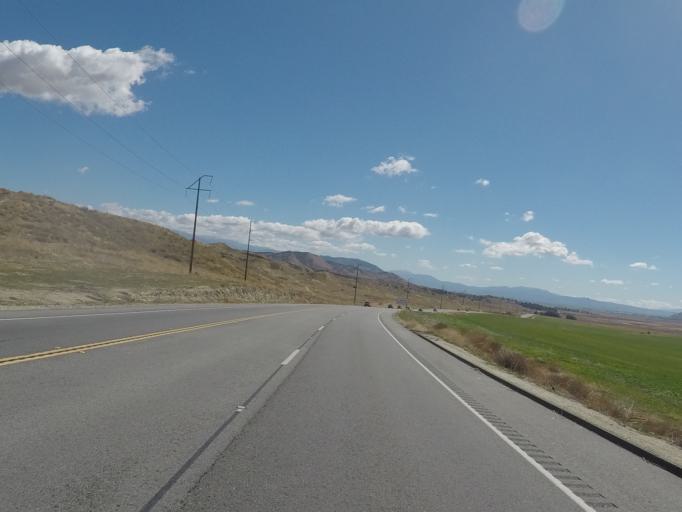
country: US
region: California
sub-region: Riverside County
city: Lakeview
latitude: 33.9185
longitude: -117.1018
